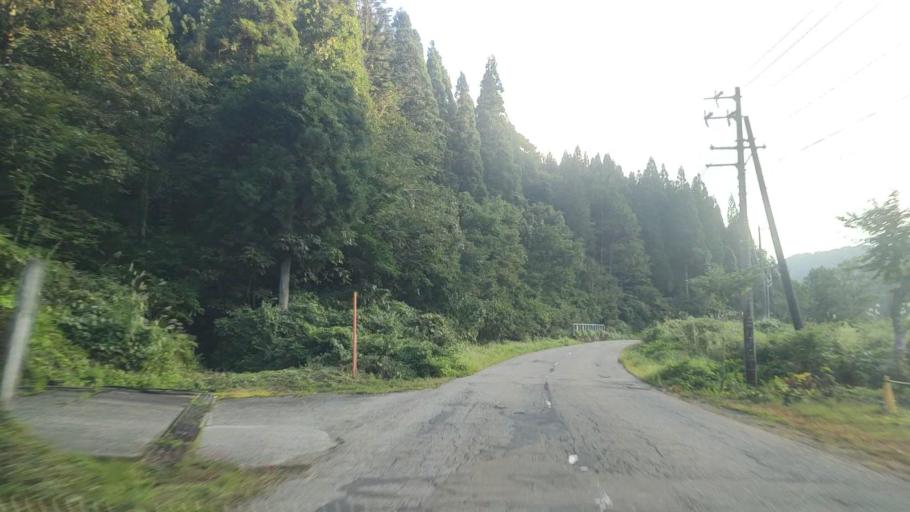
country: JP
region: Toyama
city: Yatsuomachi-higashikumisaka
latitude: 36.4659
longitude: 137.0481
